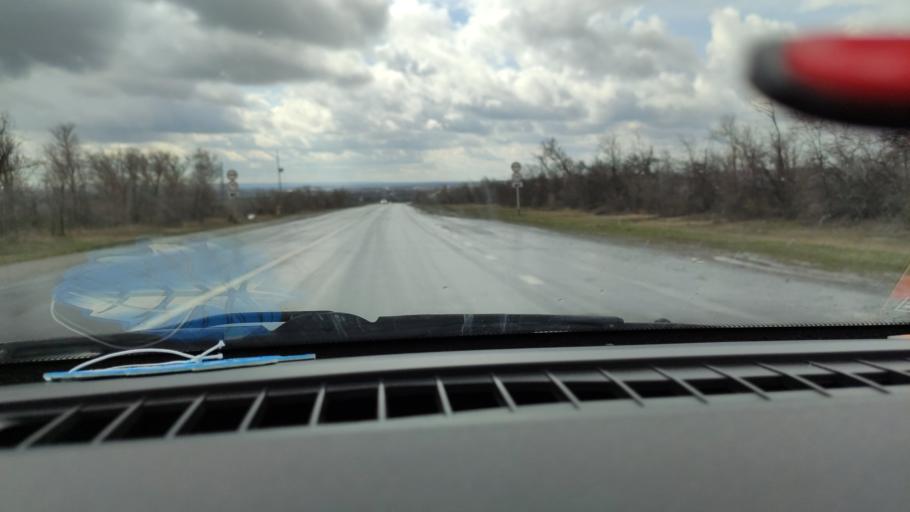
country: RU
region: Samara
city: Yelkhovka
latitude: 53.9123
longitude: 50.2653
